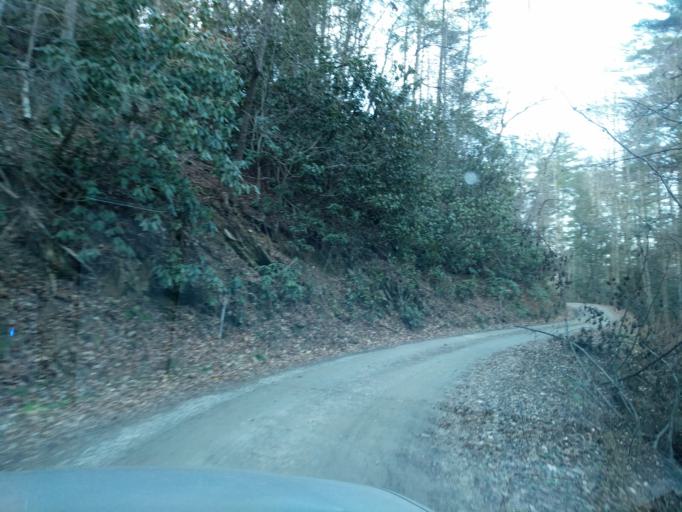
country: US
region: North Carolina
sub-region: Haywood County
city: Cove Creek
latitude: 35.7382
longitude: -83.0421
